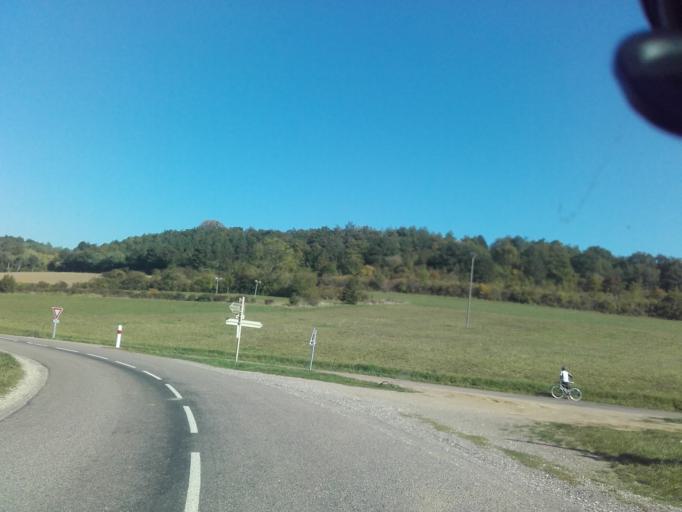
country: FR
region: Bourgogne
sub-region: Departement de la Cote-d'Or
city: Meursault
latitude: 47.0092
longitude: 4.7138
